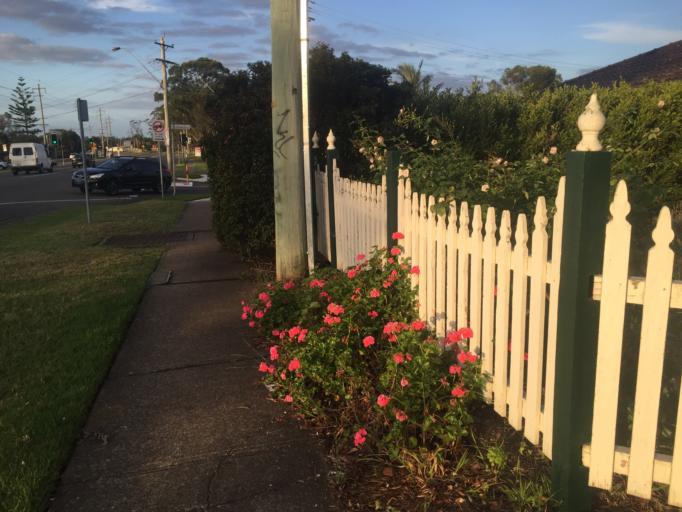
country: AU
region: New South Wales
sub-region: Blacktown
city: Blacktown
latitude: -33.7887
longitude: 150.9196
